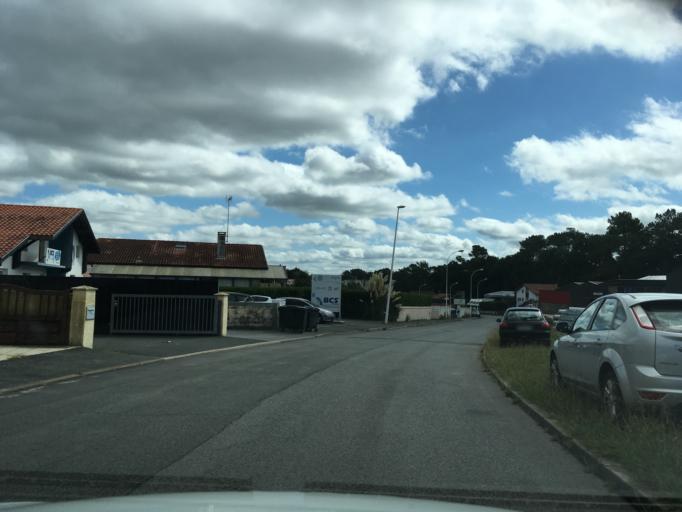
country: FR
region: Aquitaine
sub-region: Departement des Pyrenees-Atlantiques
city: Boucau
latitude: 43.5114
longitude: -1.4325
